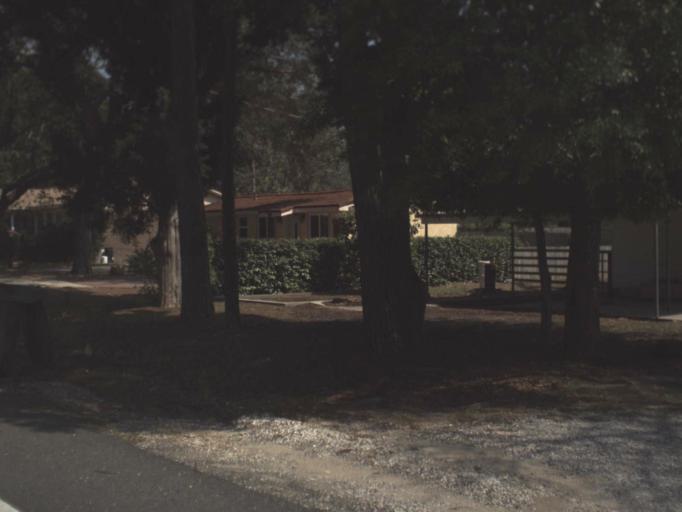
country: US
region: Florida
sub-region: Escambia County
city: Myrtle Grove
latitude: 30.3979
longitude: -87.4170
